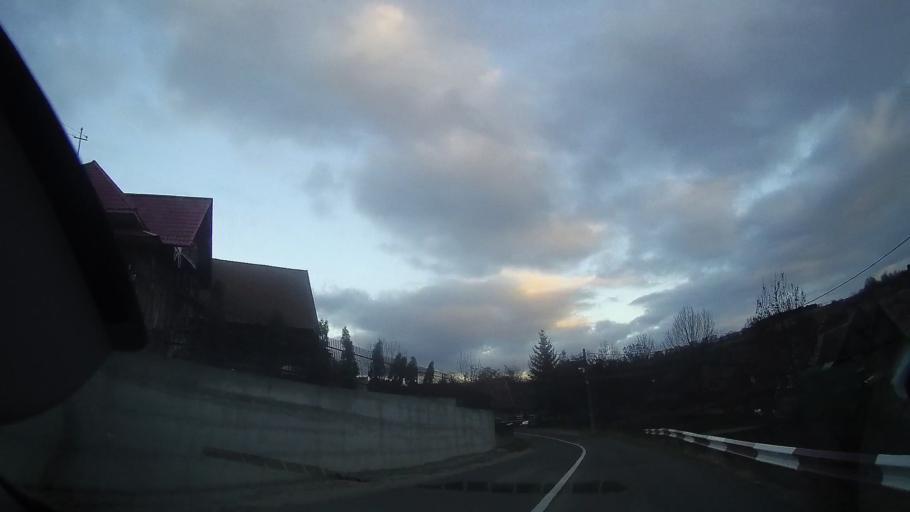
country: RO
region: Cluj
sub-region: Comuna Manastireni
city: Manastireni
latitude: 46.7817
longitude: 23.0868
